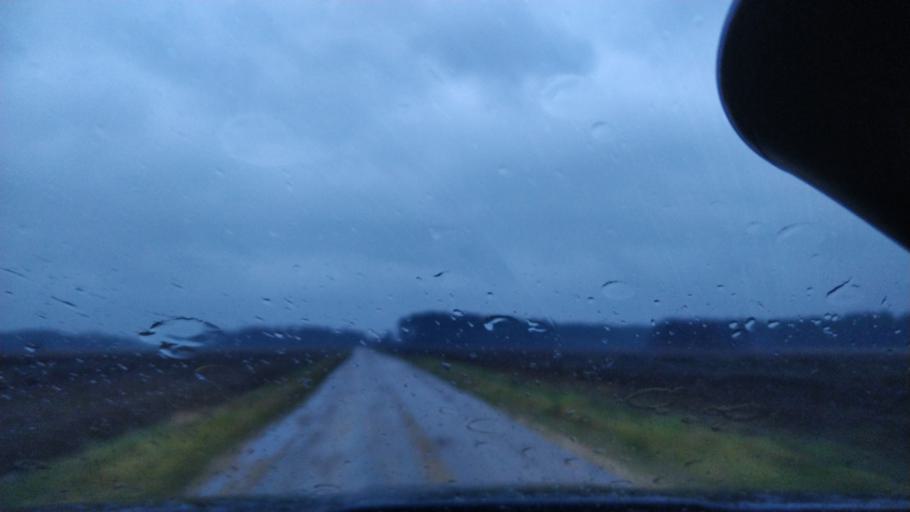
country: EE
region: Laeaene
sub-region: Lihula vald
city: Lihula
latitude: 58.8493
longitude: 23.9880
